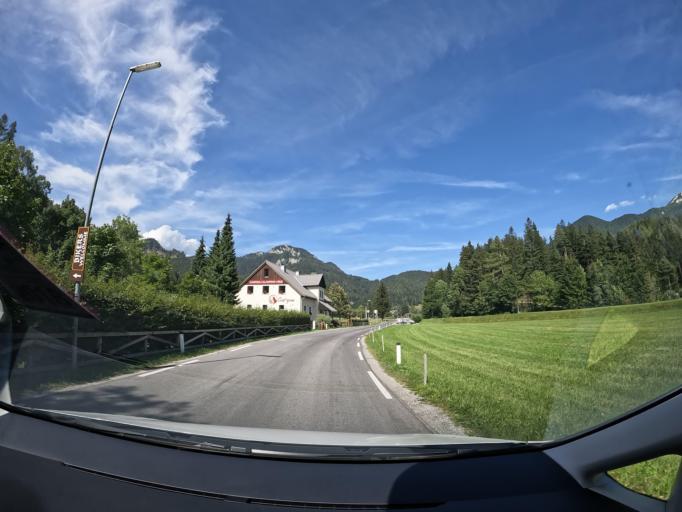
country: AT
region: Carinthia
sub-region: Politischer Bezirk Feldkirchen
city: Feldkirchen in Karnten
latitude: 46.7044
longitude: 14.1231
